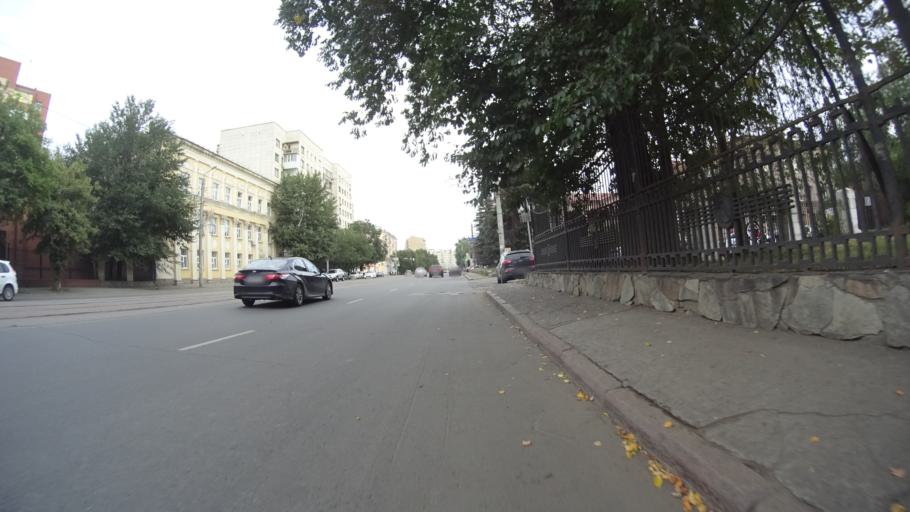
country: RU
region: Chelyabinsk
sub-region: Gorod Chelyabinsk
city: Chelyabinsk
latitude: 55.1535
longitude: 61.4082
